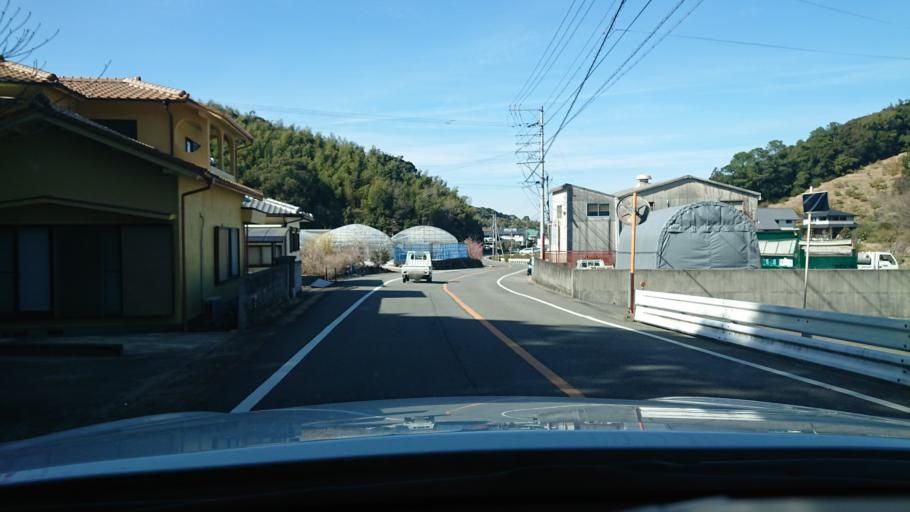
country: JP
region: Tokushima
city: Komatsushimacho
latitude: 33.9727
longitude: 134.5920
